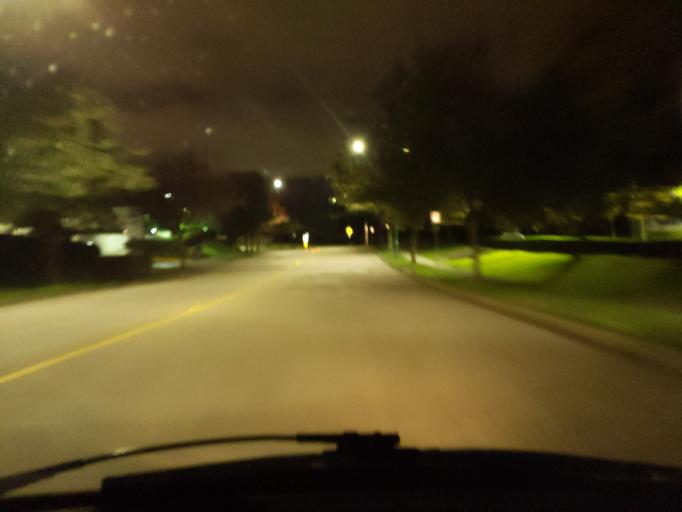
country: CA
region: British Columbia
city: Burnaby
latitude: 49.2599
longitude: -123.0113
